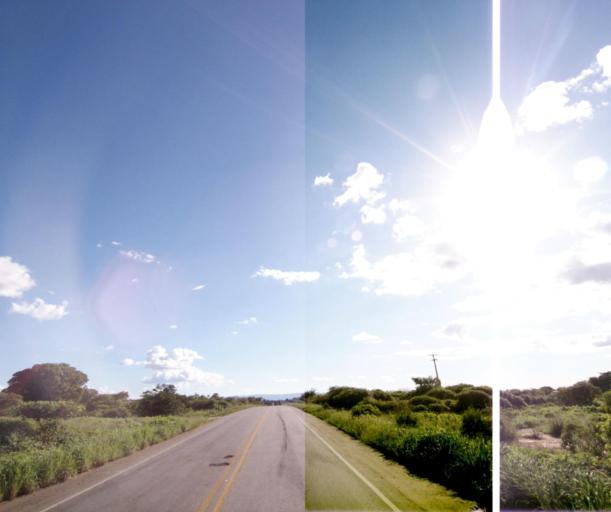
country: BR
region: Bahia
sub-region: Guanambi
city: Guanambi
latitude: -14.1701
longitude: -42.7248
